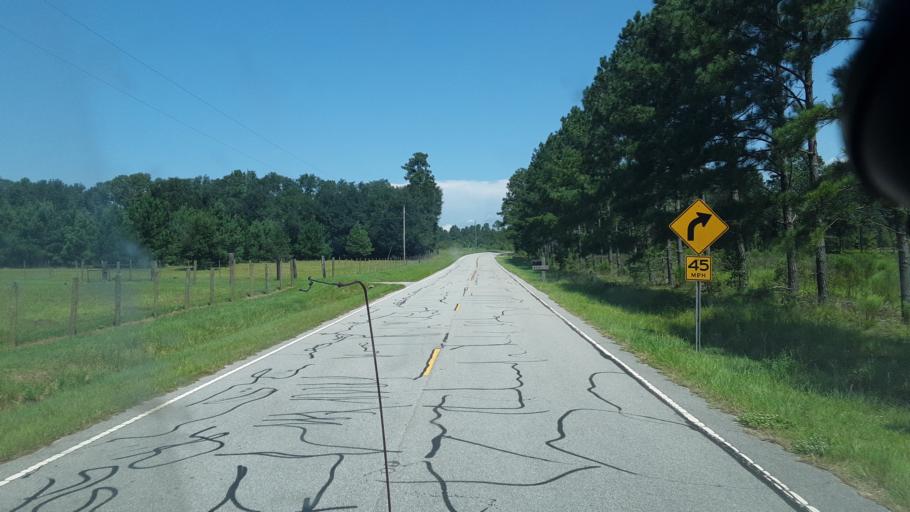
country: US
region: South Carolina
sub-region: Orangeburg County
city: Edisto
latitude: 33.6064
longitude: -81.0212
